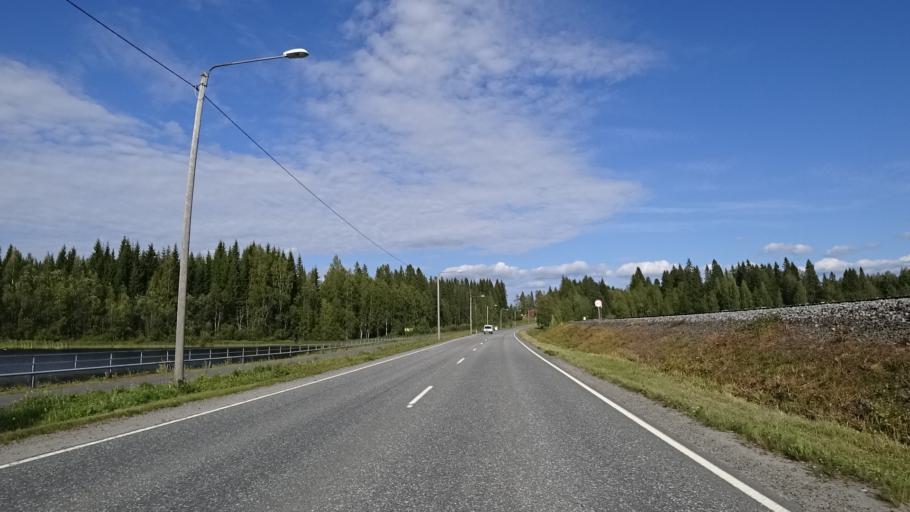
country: FI
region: North Karelia
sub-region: Joensuu
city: Eno
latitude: 62.8034
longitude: 30.1226
